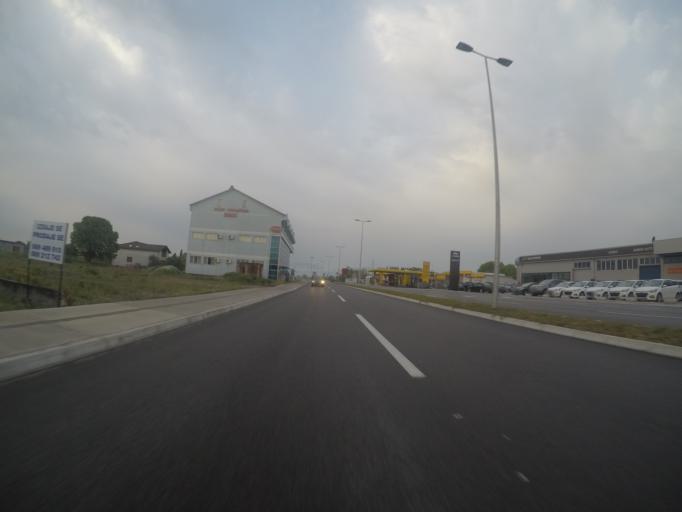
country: ME
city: Mojanovici
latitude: 42.3574
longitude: 19.2235
